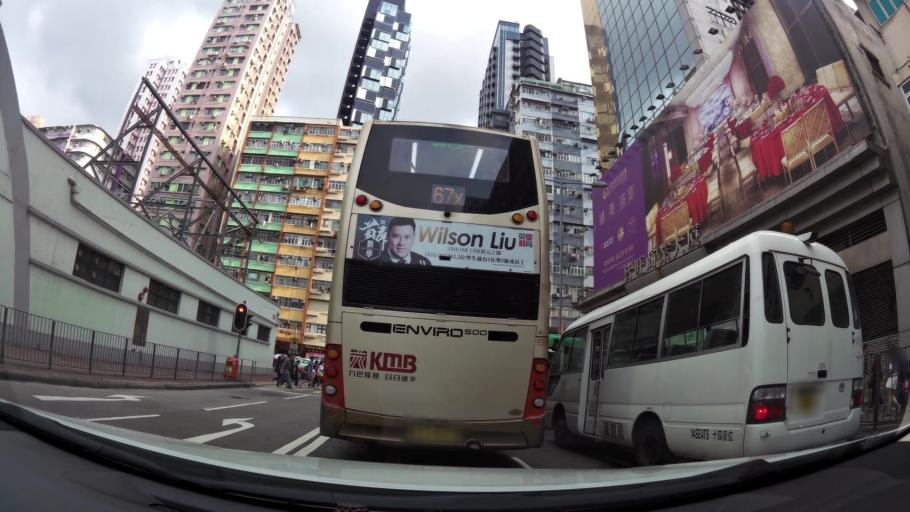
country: HK
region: Kowloon City
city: Kowloon
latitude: 22.3201
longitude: 114.1716
